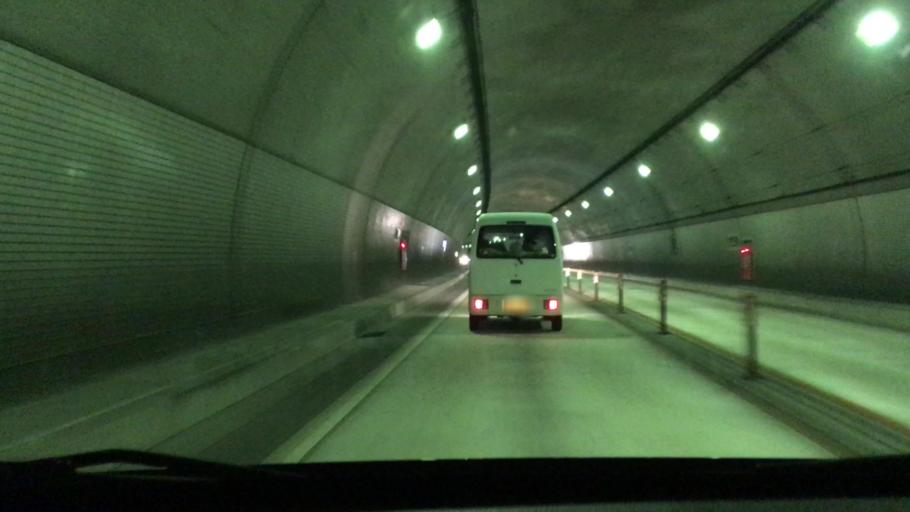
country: JP
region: Nagasaki
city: Sasebo
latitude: 33.0930
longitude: 129.7787
